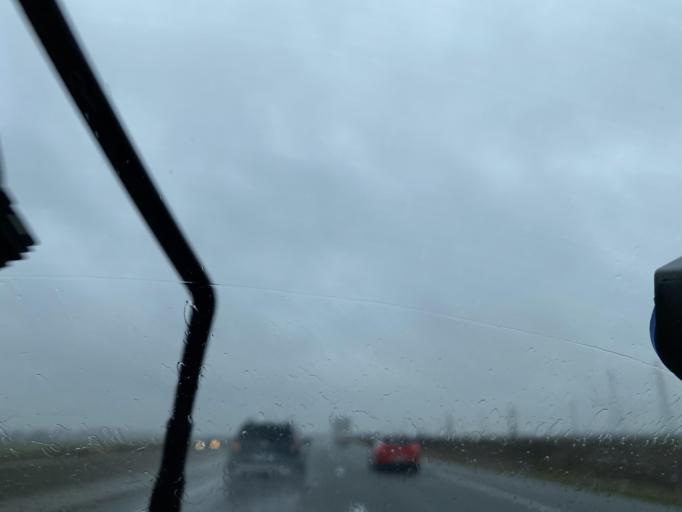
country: FR
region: Centre
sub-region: Departement d'Eure-et-Loir
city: Sours
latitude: 48.3530
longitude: 1.6180
